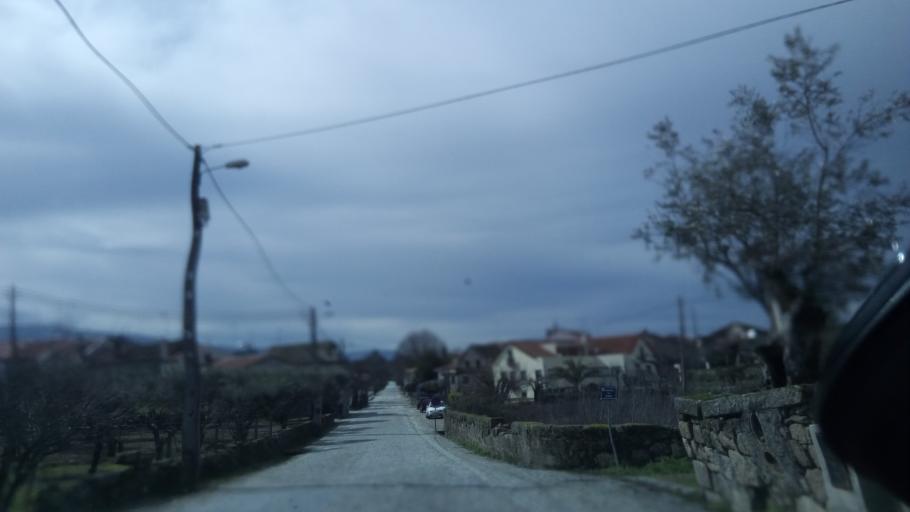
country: PT
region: Guarda
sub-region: Fornos de Algodres
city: Fornos de Algodres
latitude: 40.5884
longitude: -7.5387
